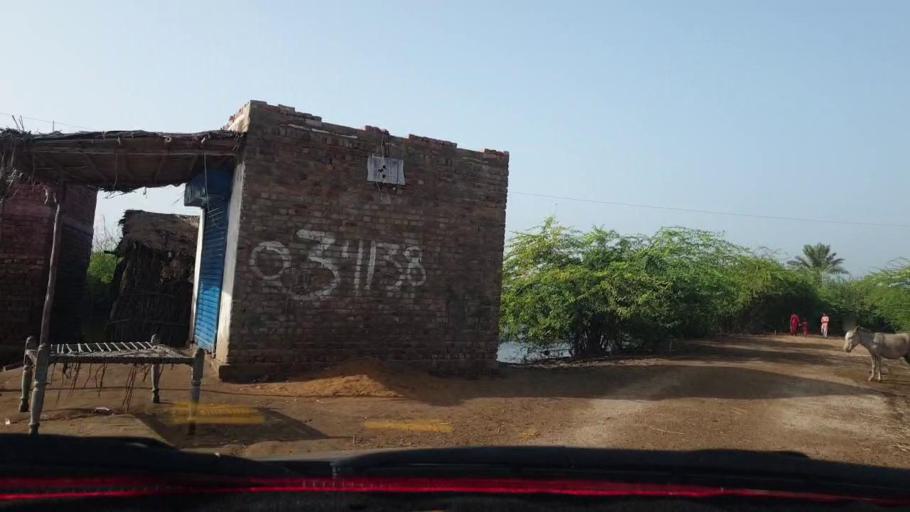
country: PK
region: Sindh
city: Talhar
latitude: 24.9245
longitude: 68.7515
